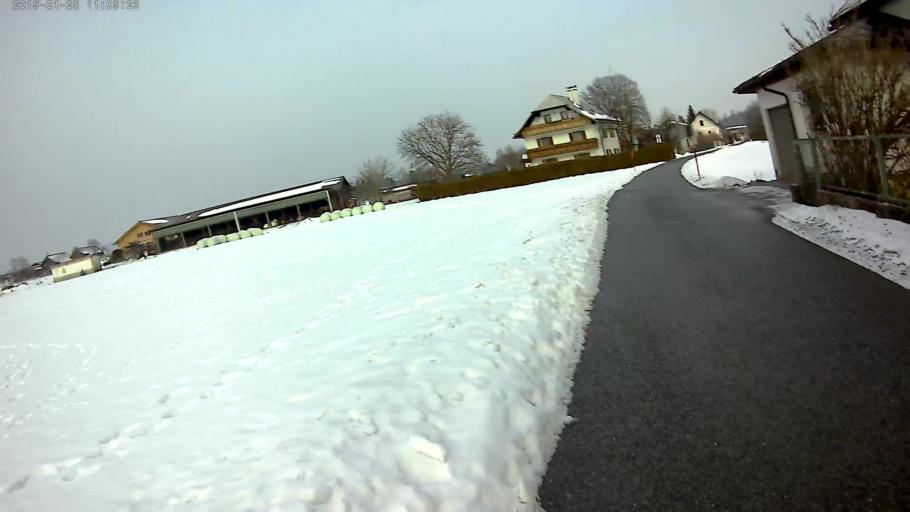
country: AT
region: Salzburg
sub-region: Politischer Bezirk Salzburg-Umgebung
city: Anif
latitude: 47.7423
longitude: 13.0618
